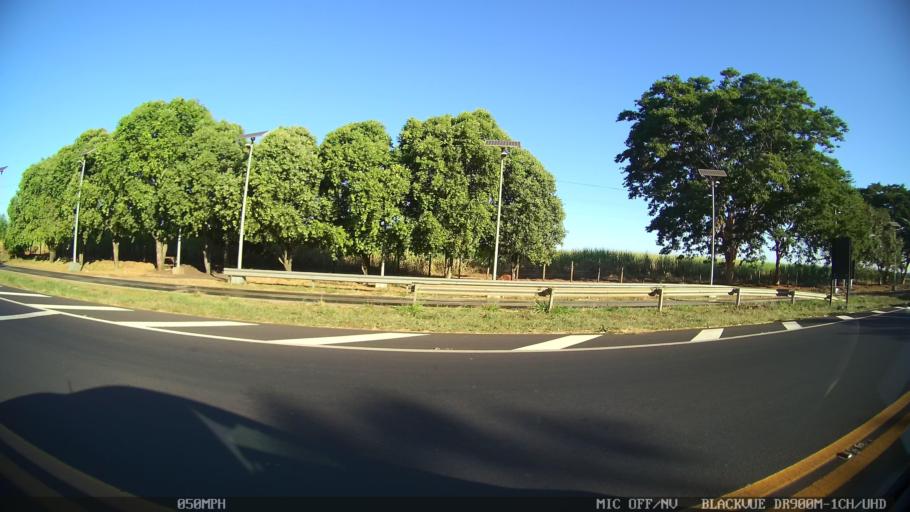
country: BR
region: Sao Paulo
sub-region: Guapiacu
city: Guapiacu
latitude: -20.7537
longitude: -49.1480
